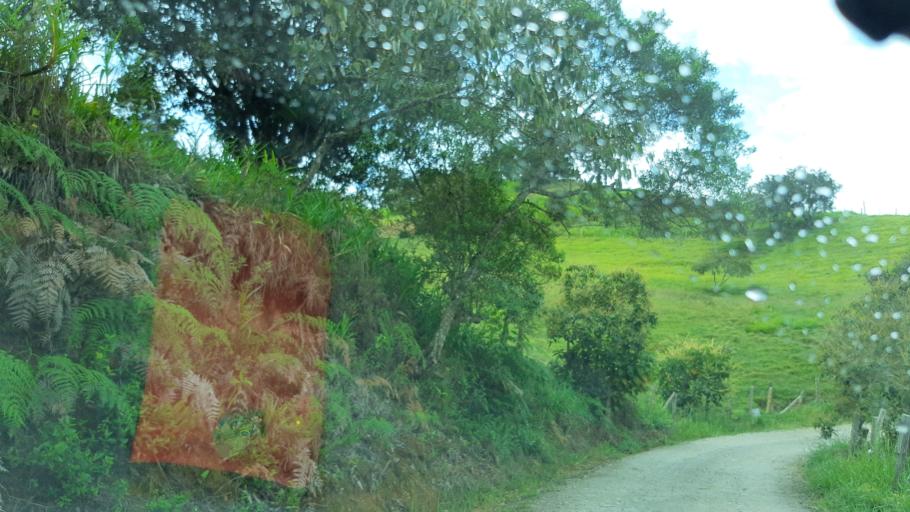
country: CO
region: Boyaca
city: Garagoa
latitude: 5.0358
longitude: -73.3653
